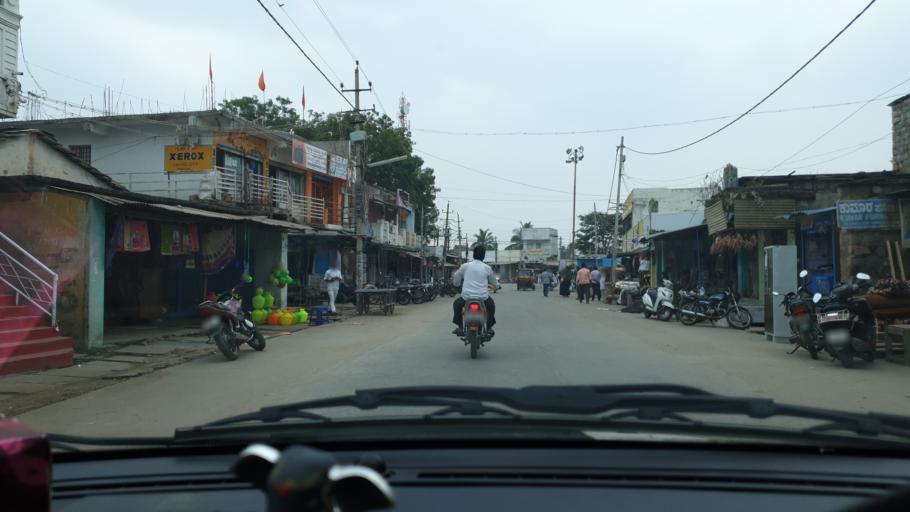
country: IN
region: Karnataka
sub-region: Yadgir
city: Gurmatkal
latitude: 16.8677
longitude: 77.3920
